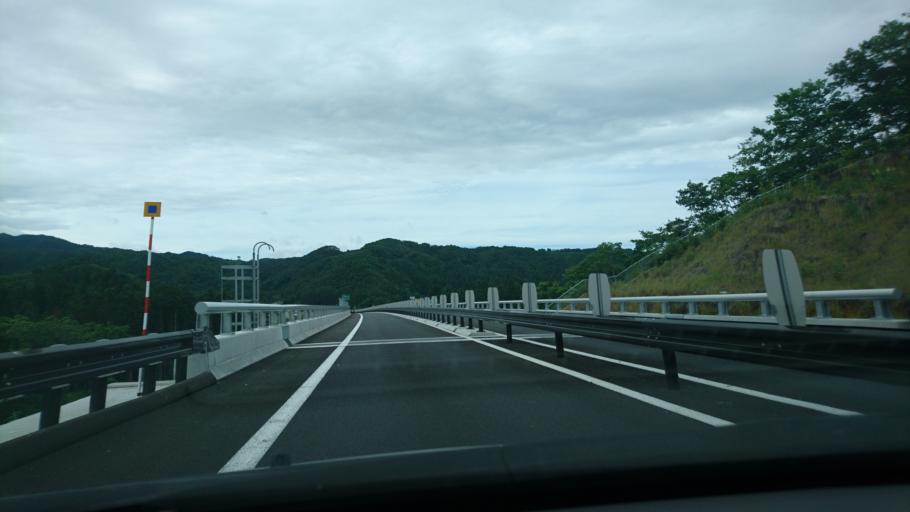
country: JP
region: Iwate
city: Miyako
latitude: 39.8364
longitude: 141.9603
